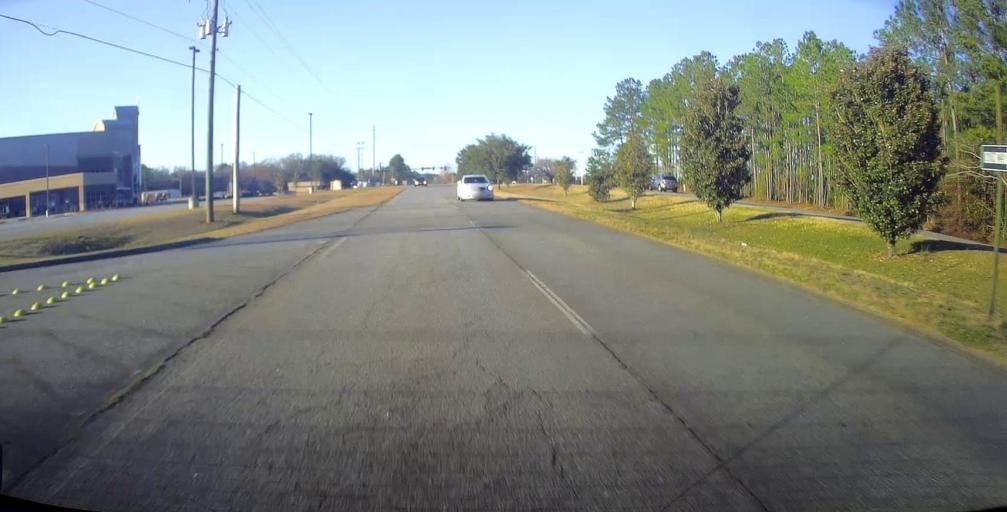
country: US
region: Georgia
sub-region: Dougherty County
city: Albany
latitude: 31.5470
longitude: -84.2242
